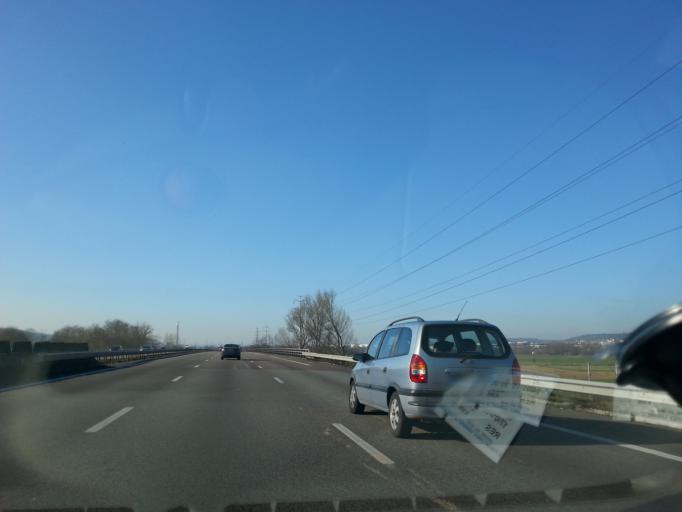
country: FR
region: Ile-de-France
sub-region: Departement des Yvelines
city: Epone
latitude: 48.9643
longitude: 1.8242
